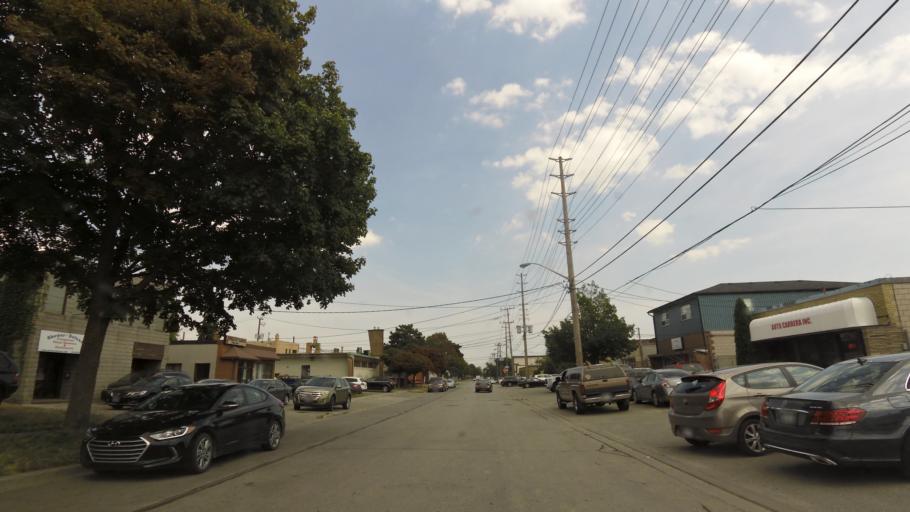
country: CA
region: Ontario
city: Etobicoke
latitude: 43.6370
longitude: -79.5320
